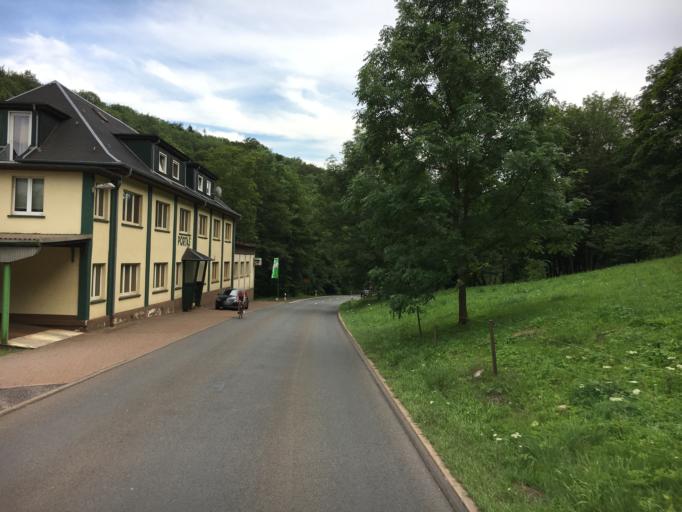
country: DE
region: Thuringia
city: Brotterode
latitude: 50.8149
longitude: 10.4295
